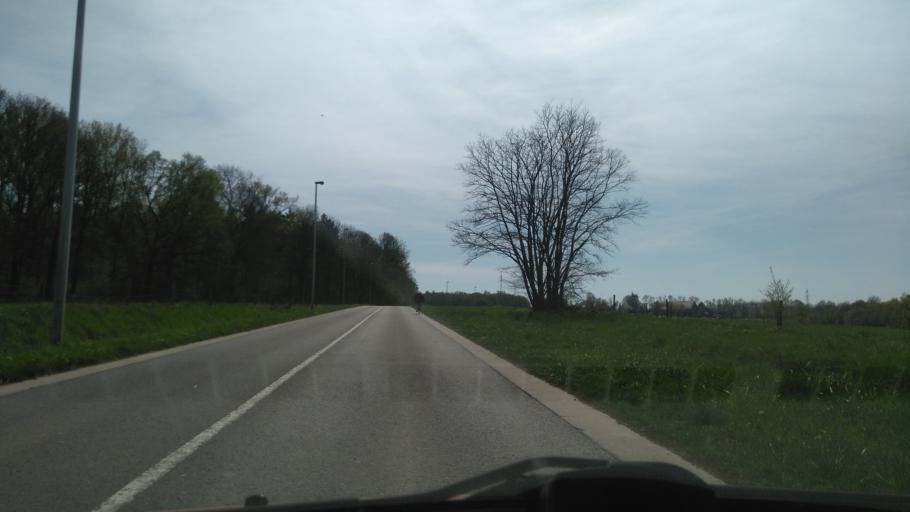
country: BE
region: Wallonia
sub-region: Province de Namur
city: Noville-les-Bois
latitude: 50.5351
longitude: 4.9805
